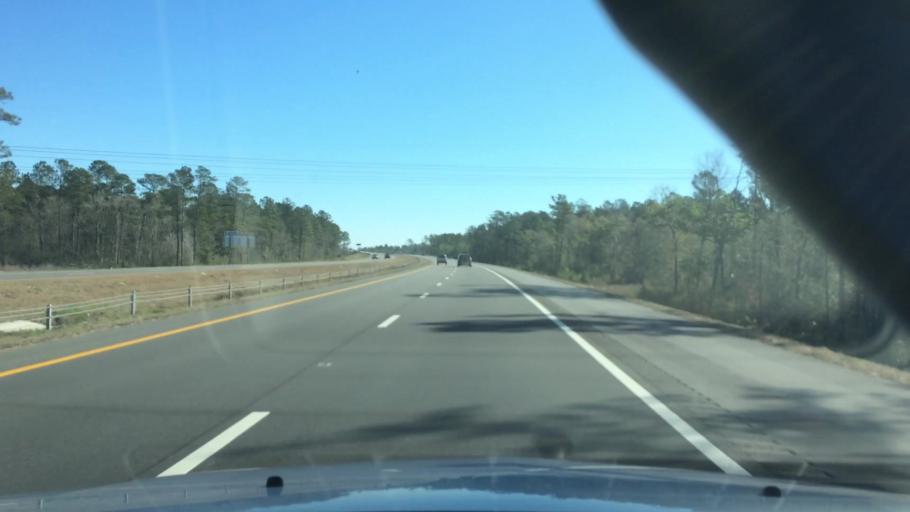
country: US
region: North Carolina
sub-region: Brunswick County
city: Leland
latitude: 34.2733
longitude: -78.0313
